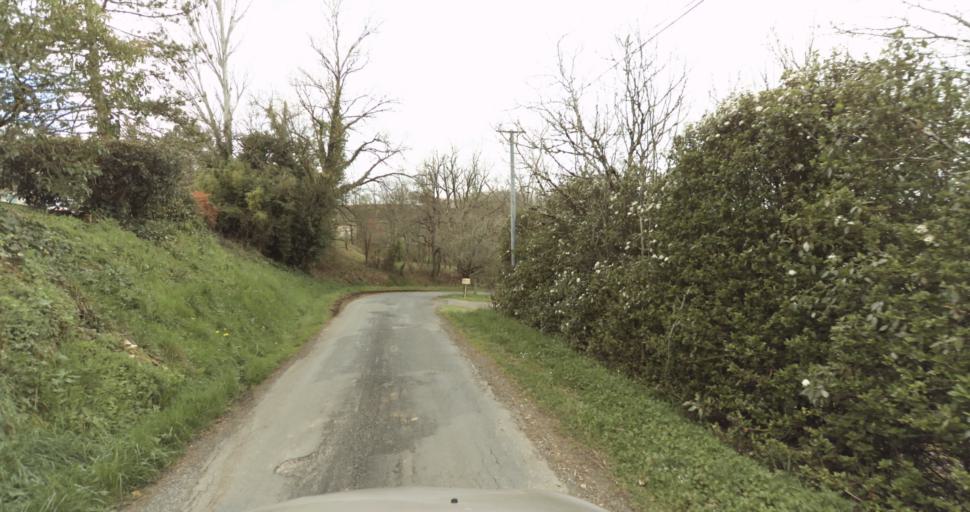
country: FR
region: Midi-Pyrenees
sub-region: Departement du Tarn
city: Puygouzon
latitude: 43.8688
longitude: 2.1727
